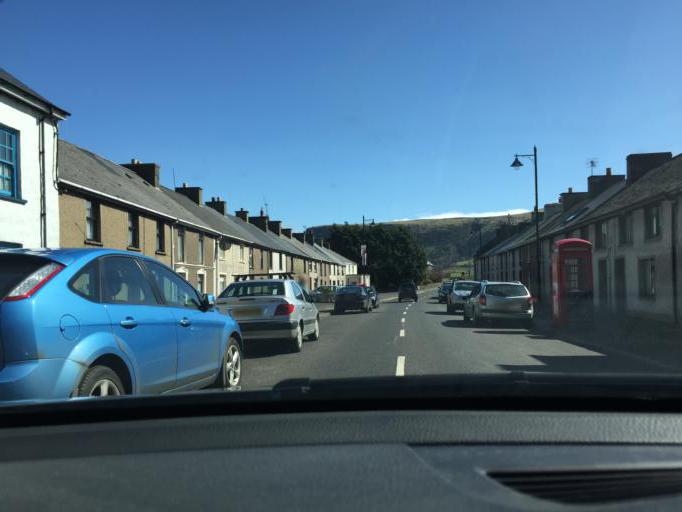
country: GB
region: Northern Ireland
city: Glenariff
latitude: 55.0610
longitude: -6.0599
